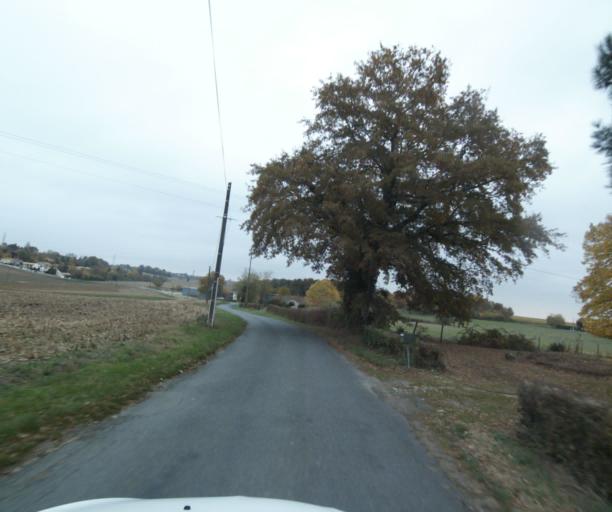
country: FR
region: Poitou-Charentes
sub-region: Departement de la Charente-Maritime
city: Les Gonds
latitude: 45.7392
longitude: -0.6004
